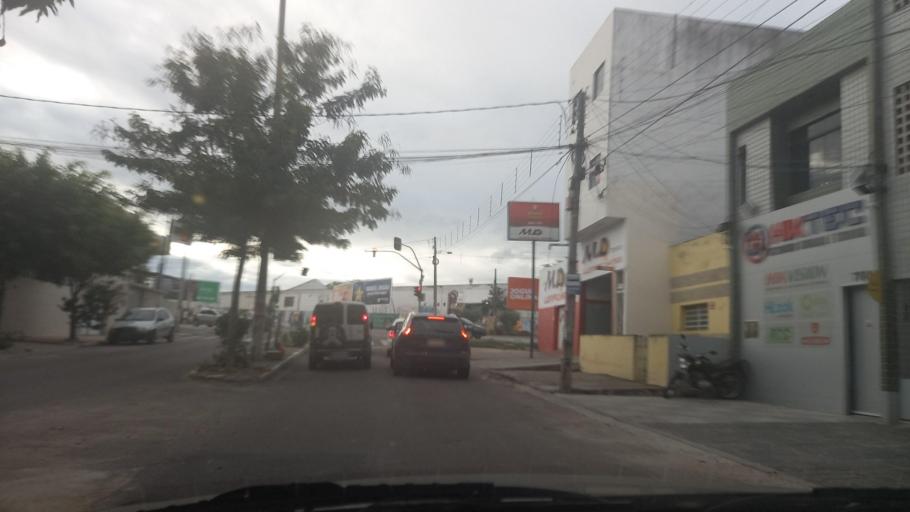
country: BR
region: Pernambuco
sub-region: Caruaru
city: Caruaru
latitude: -8.2765
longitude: -35.9796
